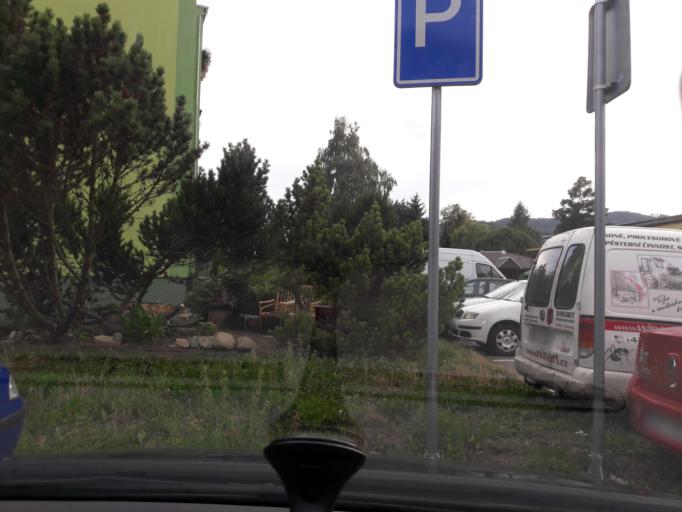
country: CZ
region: Olomoucky
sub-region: Okres Sumperk
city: Velke Losiny
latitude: 50.0284
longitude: 17.0389
